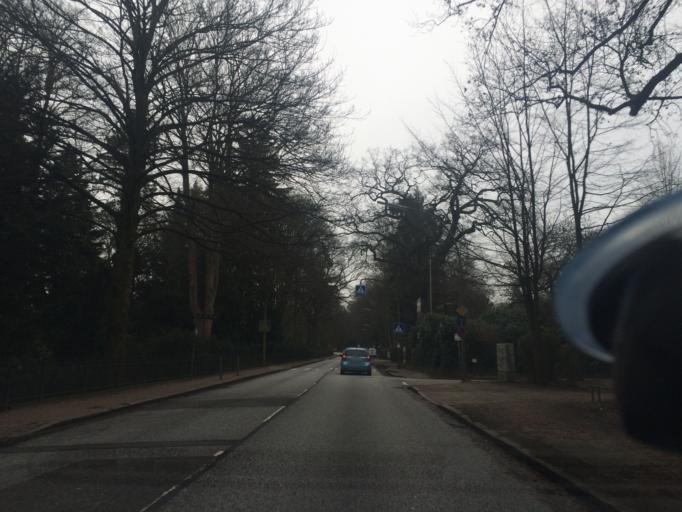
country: DE
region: Schleswig-Holstein
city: Halstenbek
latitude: 53.5566
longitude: 9.8322
